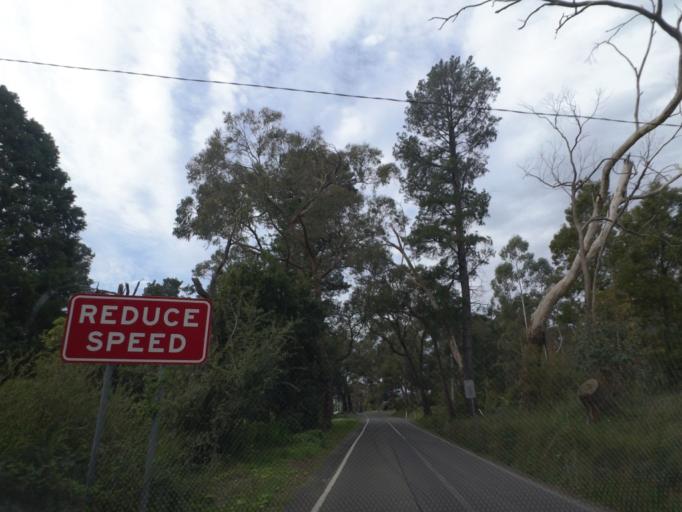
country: AU
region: Victoria
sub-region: Yarra Ranges
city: Montrose
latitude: -37.8151
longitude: 145.3512
